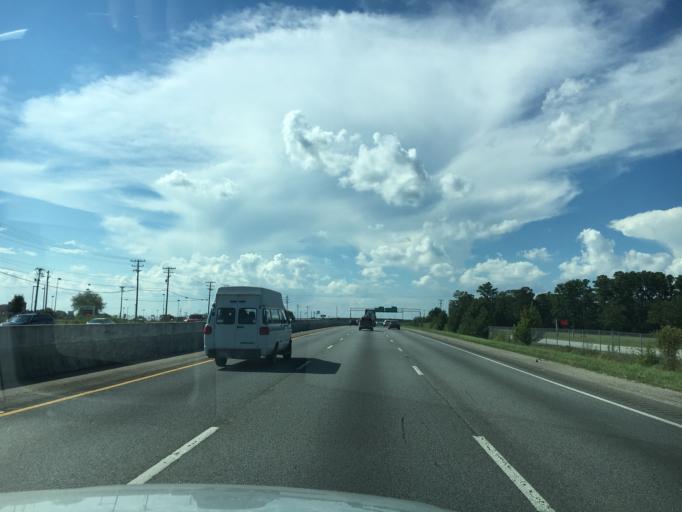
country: US
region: South Carolina
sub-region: Greenville County
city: Simpsonville
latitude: 34.7147
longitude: -82.2504
